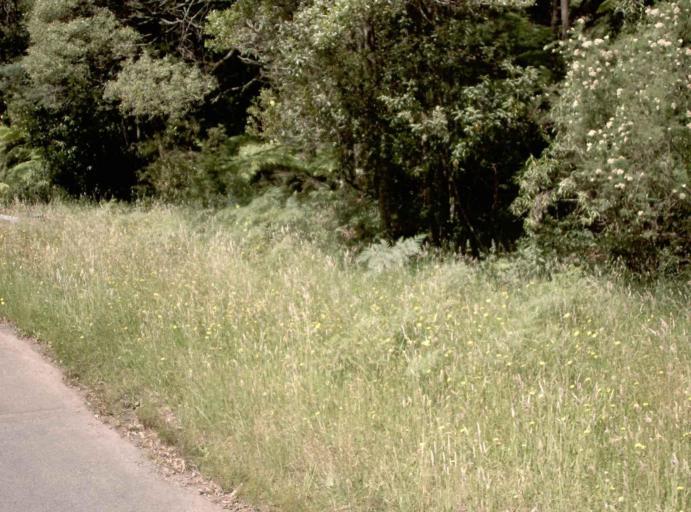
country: AU
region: Victoria
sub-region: Latrobe
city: Moe
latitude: -37.8663
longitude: 146.1225
